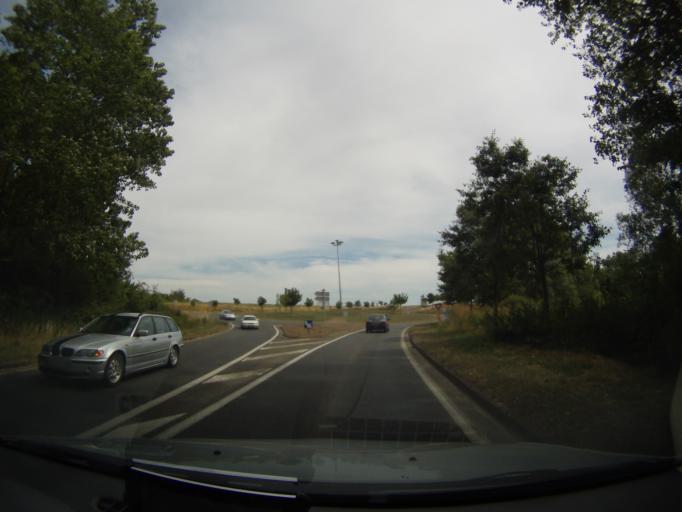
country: FR
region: Poitou-Charentes
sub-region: Departement de la Vienne
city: Mirebeau
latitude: 46.7800
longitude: 0.1344
